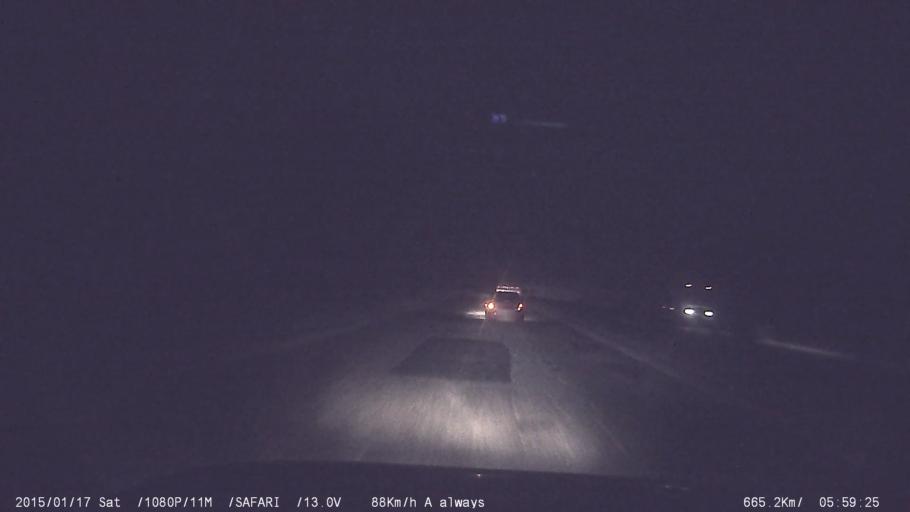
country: IN
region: Tamil Nadu
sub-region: Kancheepuram
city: Kanchipuram
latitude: 12.8979
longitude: 79.5655
